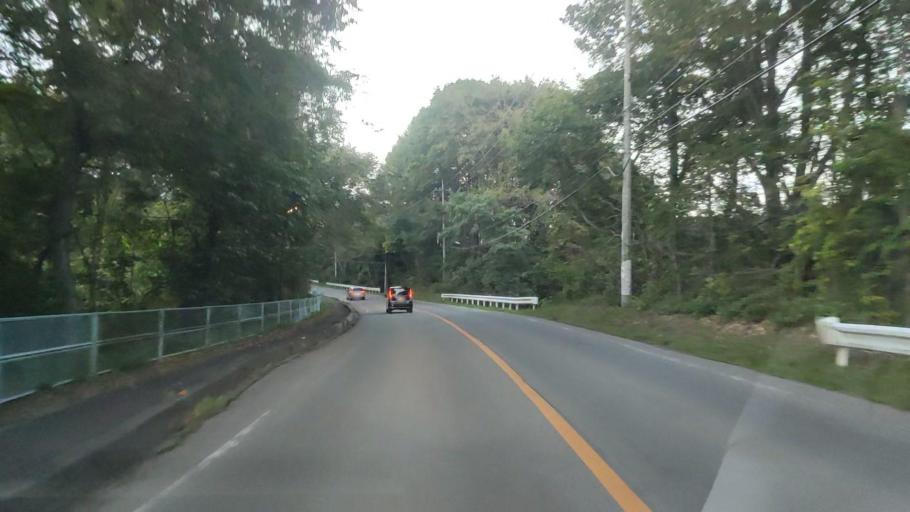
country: JP
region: Nagano
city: Komoro
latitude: 36.4917
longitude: 138.5839
